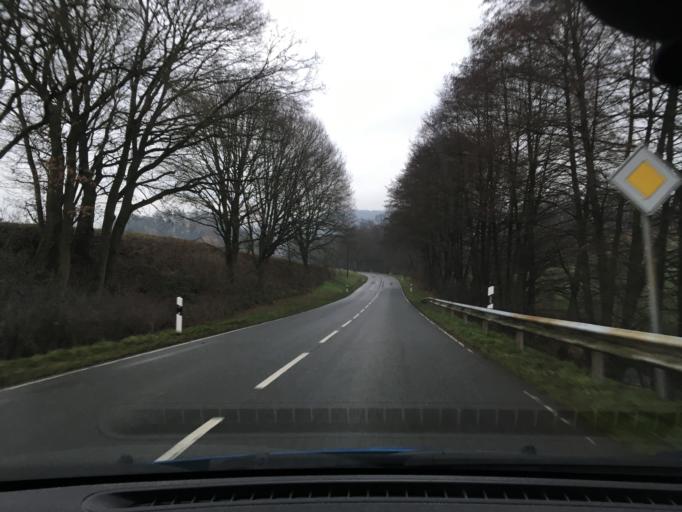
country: DE
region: Lower Saxony
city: Hardegsen
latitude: 51.6321
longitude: 9.7914
